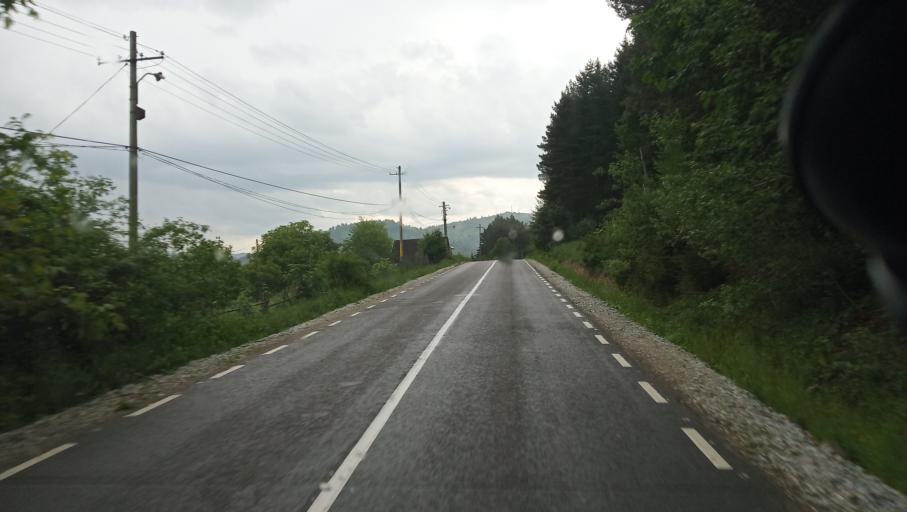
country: RO
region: Neamt
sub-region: Comuna Ceahlau
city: Ceahlau
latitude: 47.0526
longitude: 25.9367
